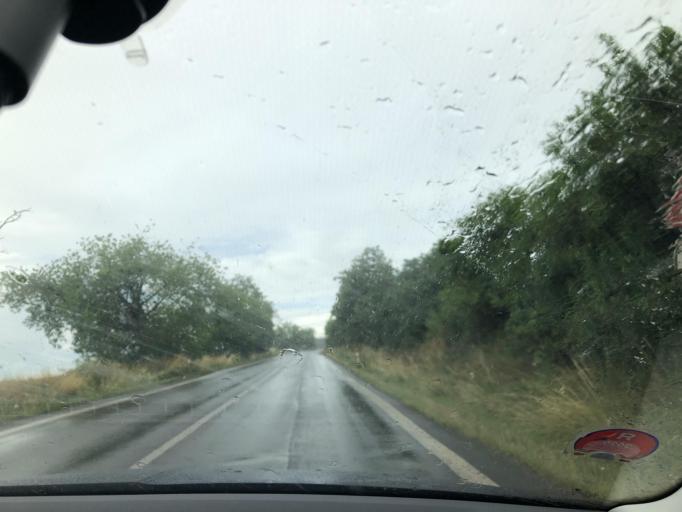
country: CZ
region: Central Bohemia
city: Velke Prilepy
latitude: 50.1521
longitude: 14.3199
